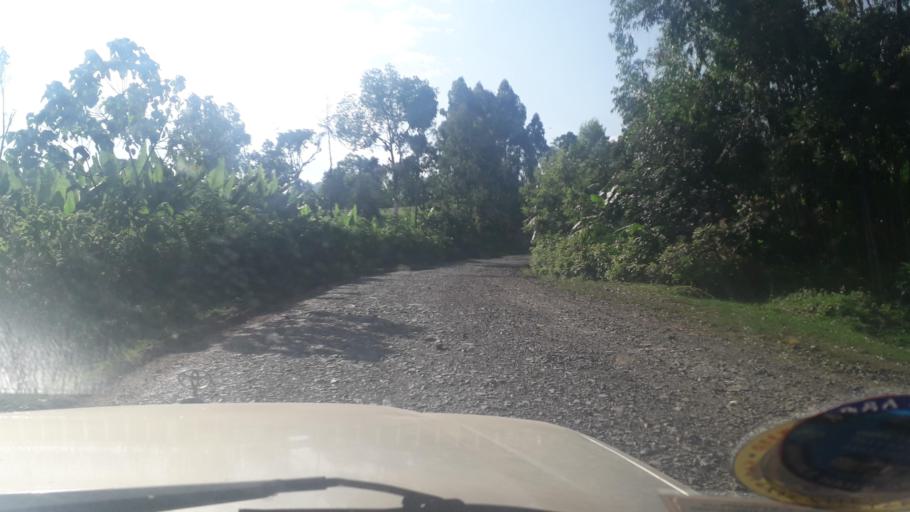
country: ET
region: Oromiya
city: Jima
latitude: 7.3858
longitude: 36.8636
